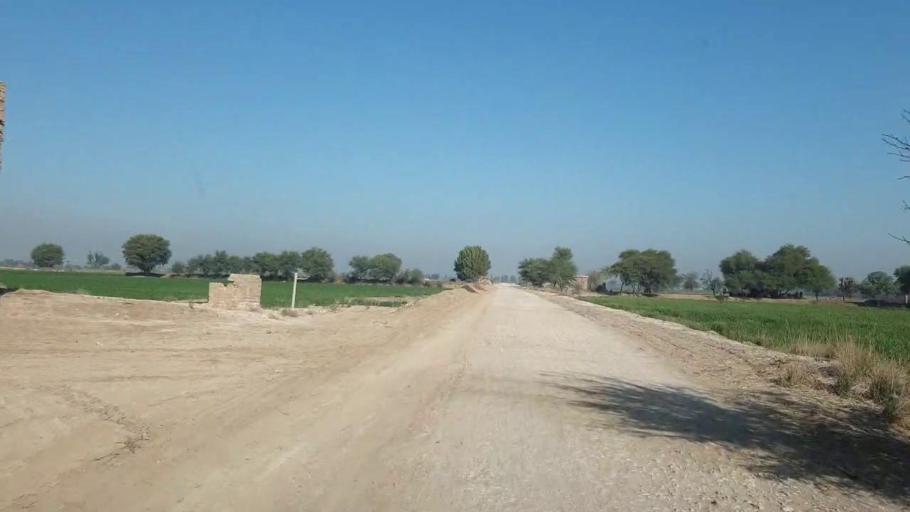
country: PK
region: Sindh
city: Shahdadpur
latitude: 25.9989
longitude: 68.4931
